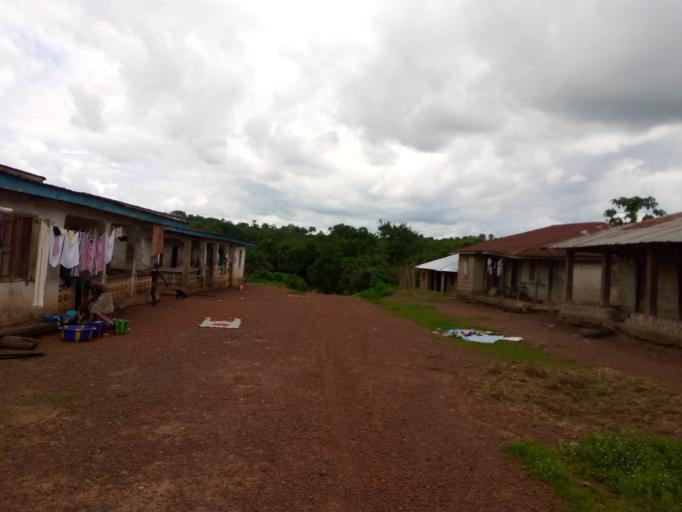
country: SL
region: Northern Province
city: Mange
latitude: 8.9869
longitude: -12.7168
